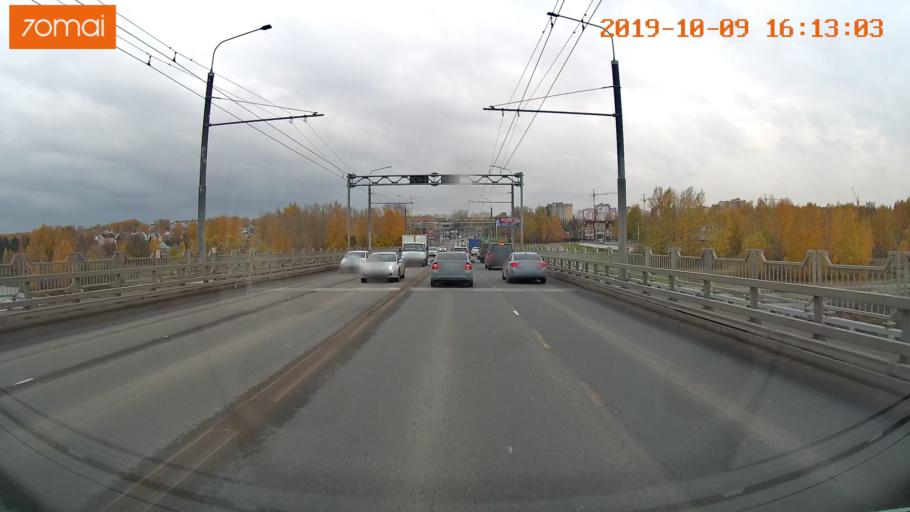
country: RU
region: Kostroma
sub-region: Kostromskoy Rayon
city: Kostroma
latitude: 57.7491
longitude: 40.9335
